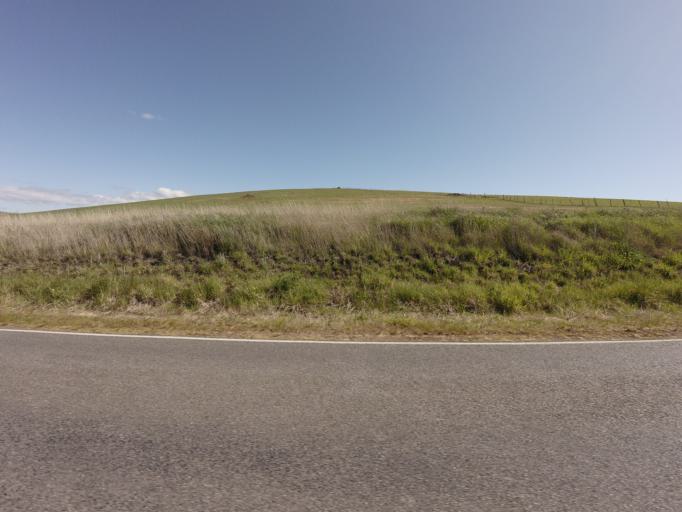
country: AU
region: Tasmania
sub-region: Derwent Valley
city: New Norfolk
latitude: -42.6460
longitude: 146.9240
